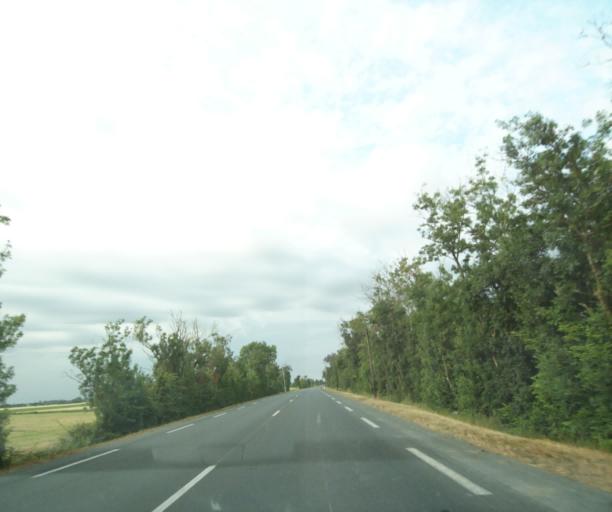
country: FR
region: Poitou-Charentes
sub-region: Departement de la Charente-Maritime
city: Marans
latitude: 46.3557
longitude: -0.9929
